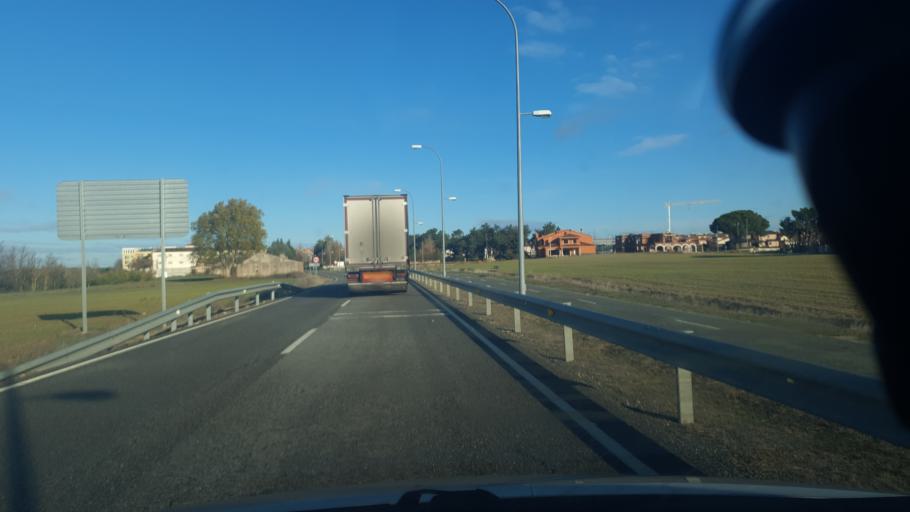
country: ES
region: Castille and Leon
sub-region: Provincia de Avila
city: Arevalo
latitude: 41.0491
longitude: -4.7182
